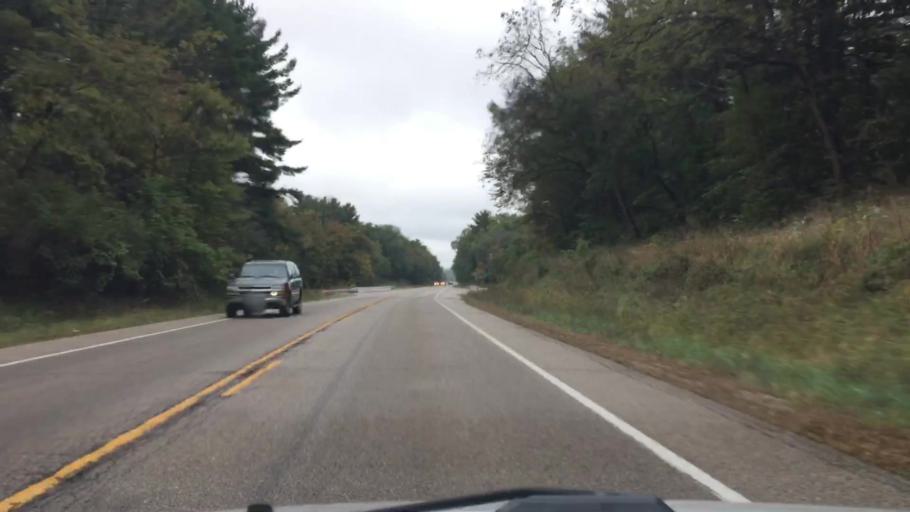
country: US
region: Wisconsin
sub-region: Rock County
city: Janesville
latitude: 42.7169
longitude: -89.0310
